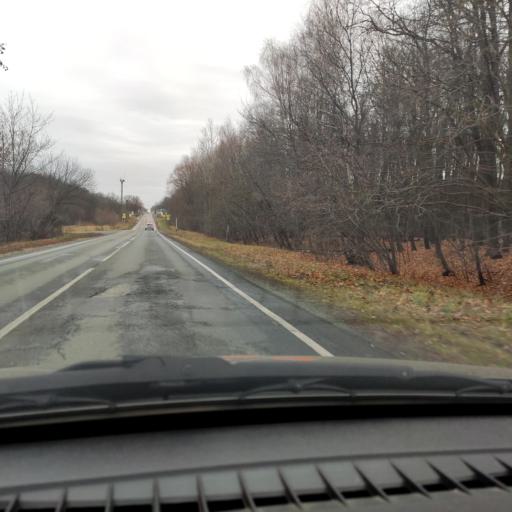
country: RU
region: Samara
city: Zhigulevsk
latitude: 53.3410
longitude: 49.4609
